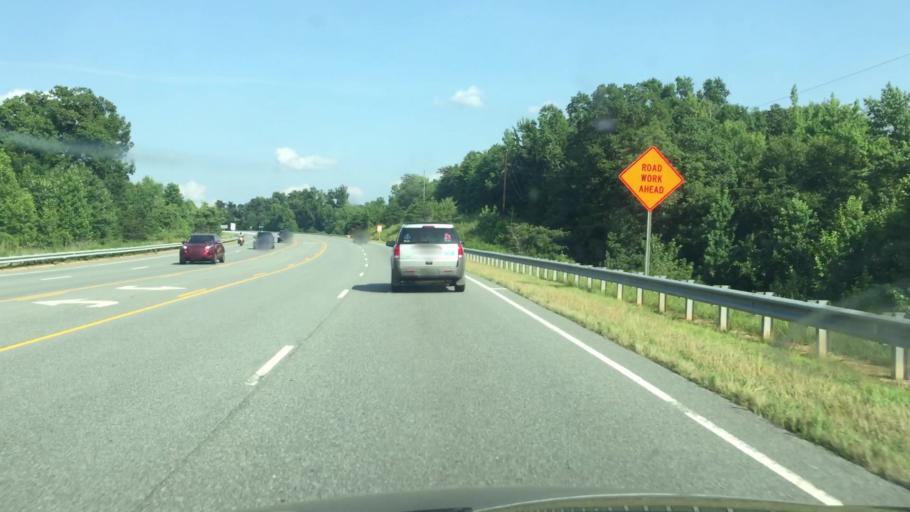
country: US
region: North Carolina
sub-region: Rockingham County
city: Reidsville
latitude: 36.3631
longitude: -79.6385
